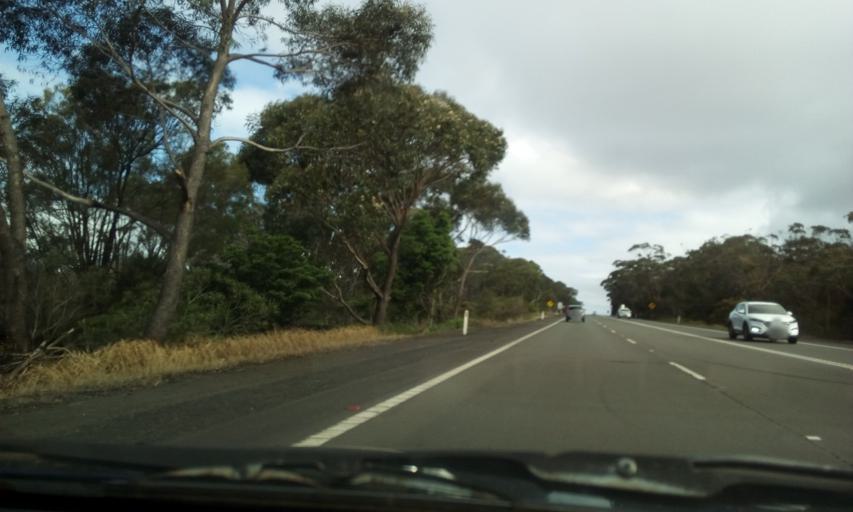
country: AU
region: New South Wales
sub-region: Wollongong
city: Bulli
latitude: -34.2936
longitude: 150.9038
